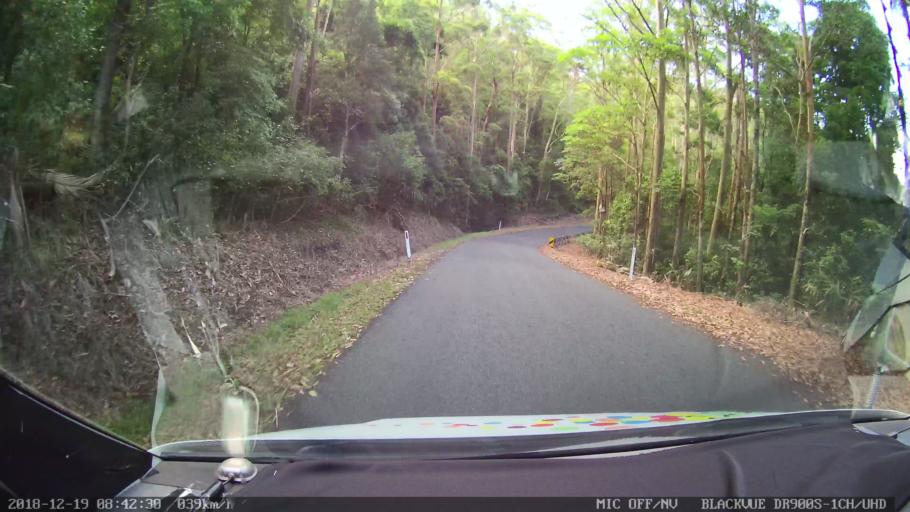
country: AU
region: New South Wales
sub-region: Kyogle
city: Kyogle
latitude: -28.3451
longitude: 152.9722
